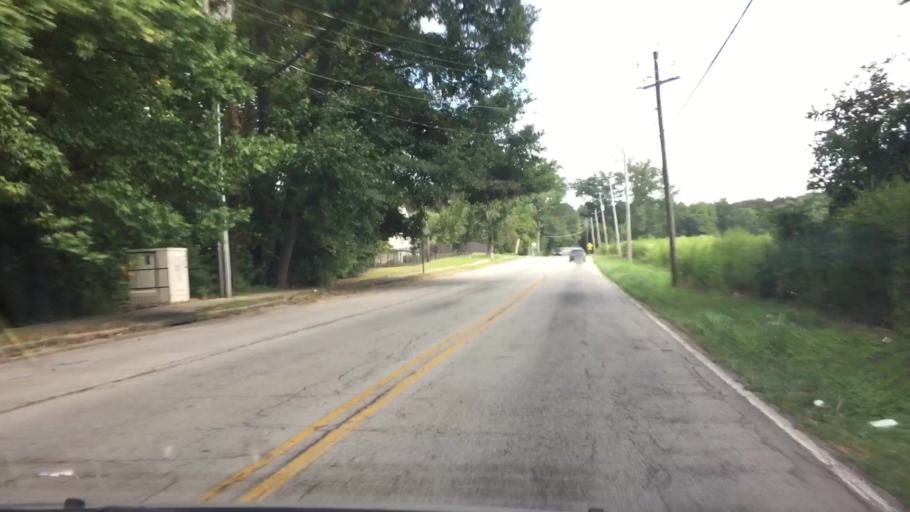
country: US
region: Georgia
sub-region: DeKalb County
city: Gresham Park
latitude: 33.6997
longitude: -84.3256
